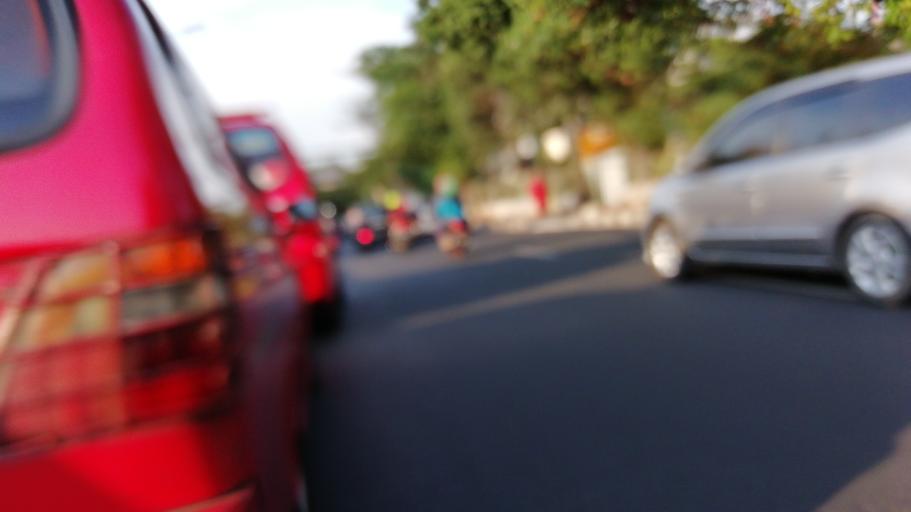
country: ID
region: Jakarta Raya
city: Jakarta
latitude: -6.3081
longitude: 106.8385
